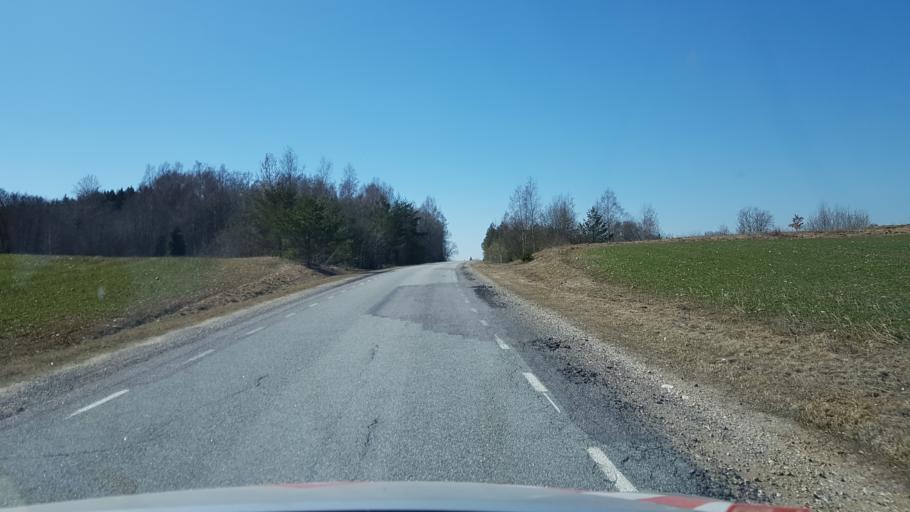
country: EE
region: Laeaene-Virumaa
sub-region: Rakke vald
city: Rakke
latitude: 59.0078
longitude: 26.3296
